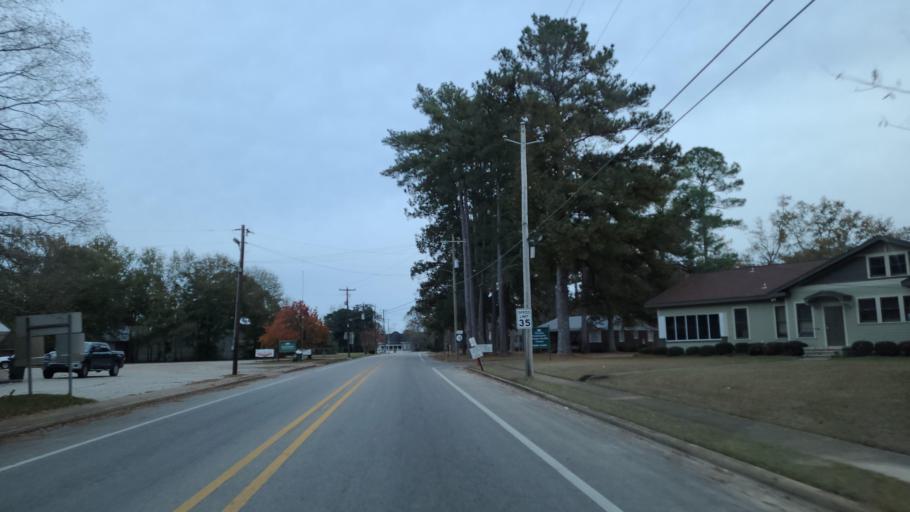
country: US
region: Mississippi
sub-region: Clarke County
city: Quitman
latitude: 32.0377
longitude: -88.7275
